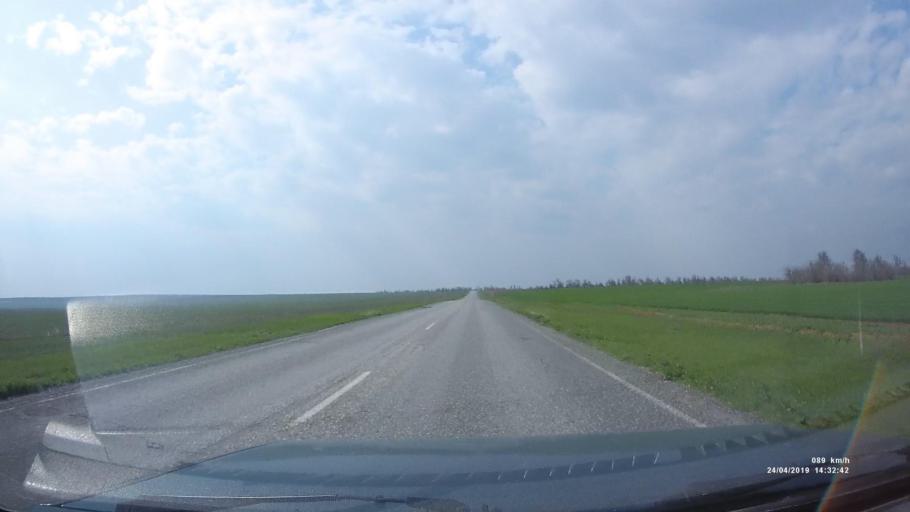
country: RU
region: Kalmykiya
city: Arshan'
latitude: 46.3669
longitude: 43.9650
